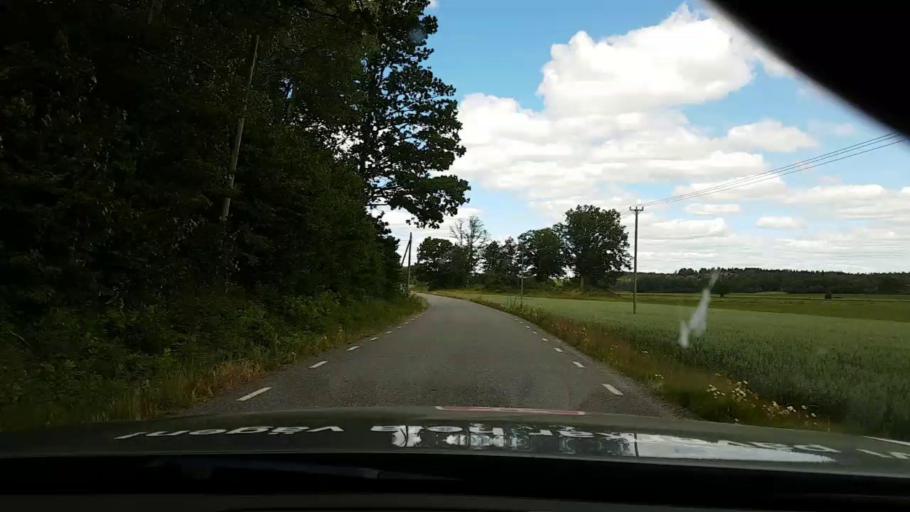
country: SE
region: Kalmar
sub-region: Vasterviks Kommun
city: Forserum
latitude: 57.9892
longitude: 16.6052
